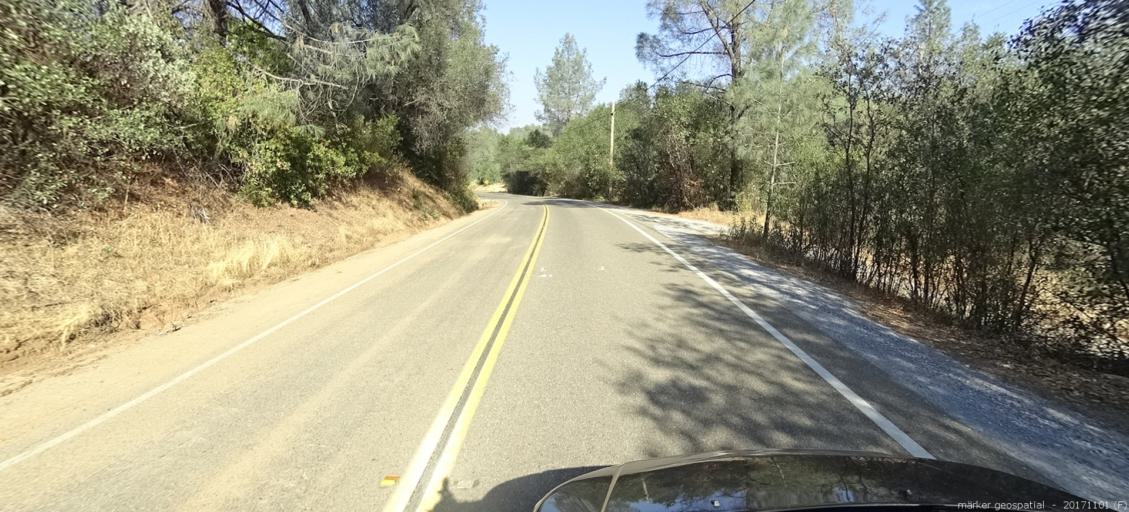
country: US
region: California
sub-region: Shasta County
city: Shasta Lake
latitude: 40.6852
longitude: -122.3157
